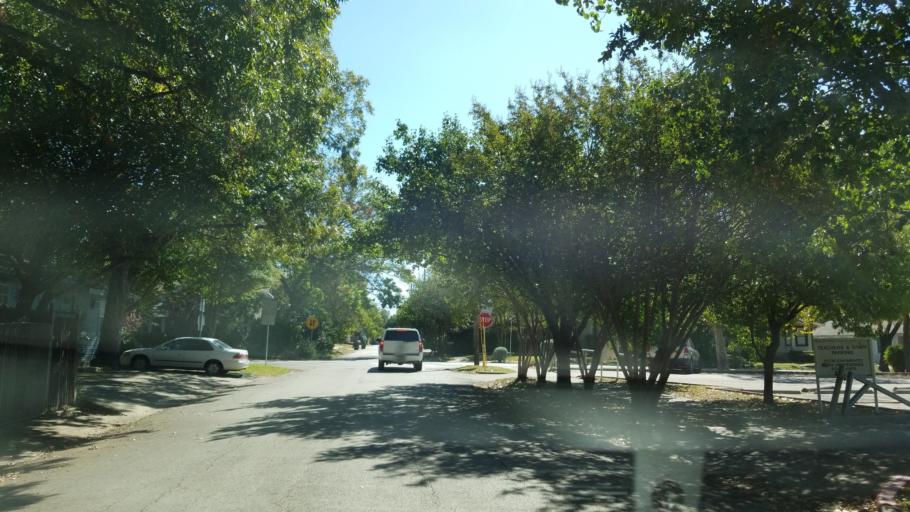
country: US
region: Texas
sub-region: Dallas County
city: Highland Park
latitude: 32.8077
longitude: -96.7563
